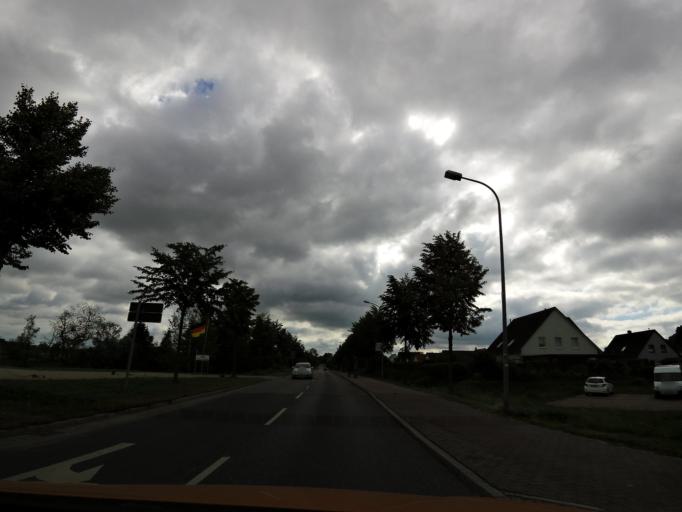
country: DE
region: Mecklenburg-Vorpommern
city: Guestrow
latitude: 53.7845
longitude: 12.1882
